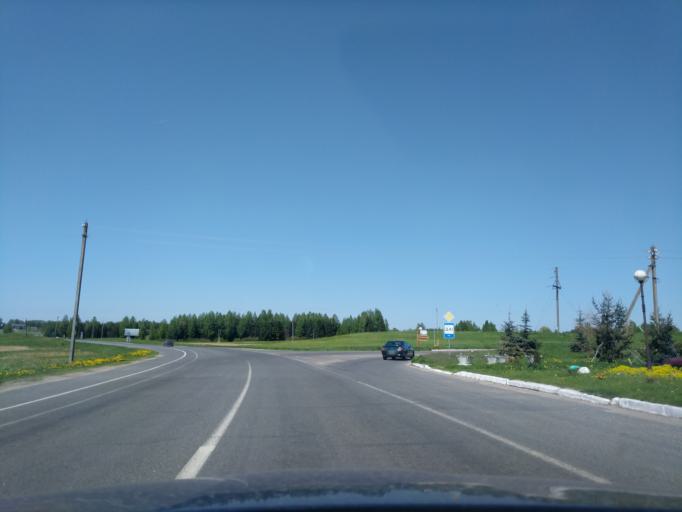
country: BY
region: Minsk
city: Myadzyel
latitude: 54.8851
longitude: 26.9367
